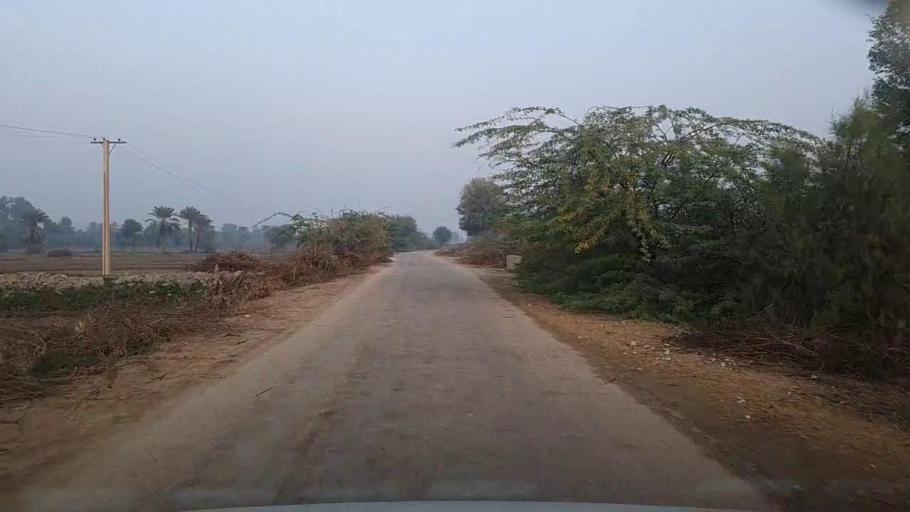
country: PK
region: Sindh
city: Kandiari
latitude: 27.0412
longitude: 68.5848
